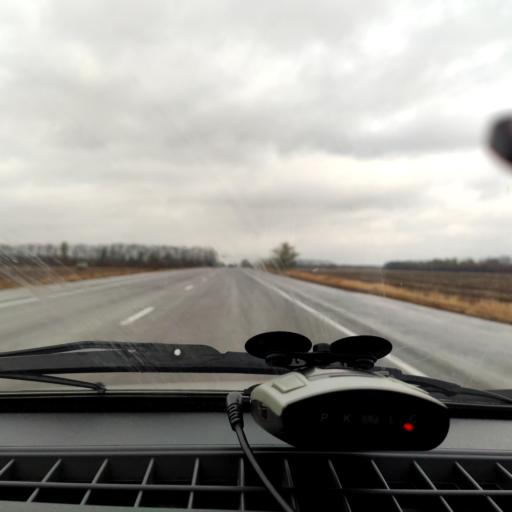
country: RU
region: Voronezj
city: Strelitsa
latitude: 51.5025
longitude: 38.9656
